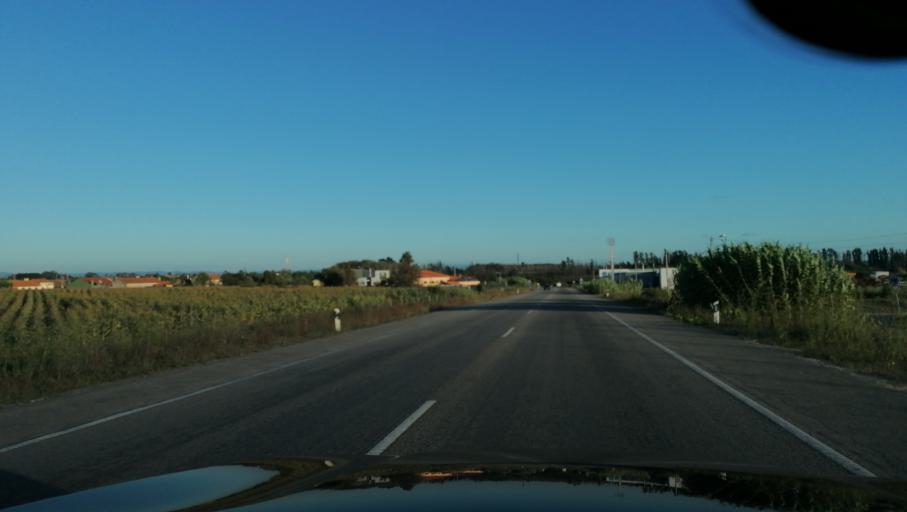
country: PT
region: Aveiro
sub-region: Aveiro
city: Oliveirinha
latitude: 40.5883
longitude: -8.6081
